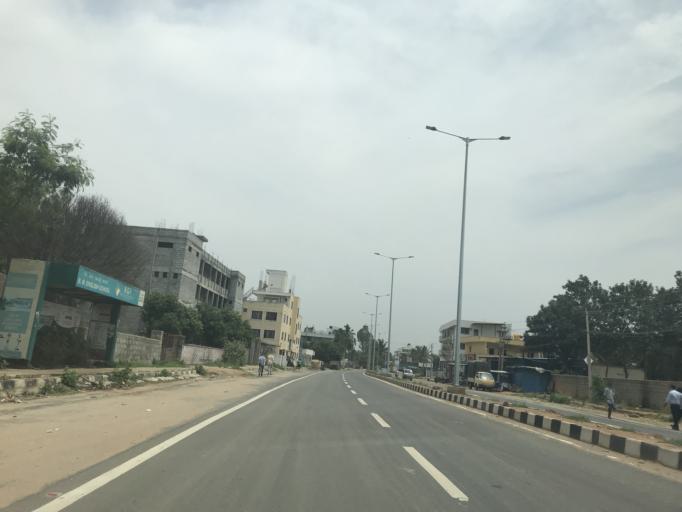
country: IN
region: Karnataka
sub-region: Bangalore Urban
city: Yelahanka
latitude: 13.1076
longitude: 77.6657
